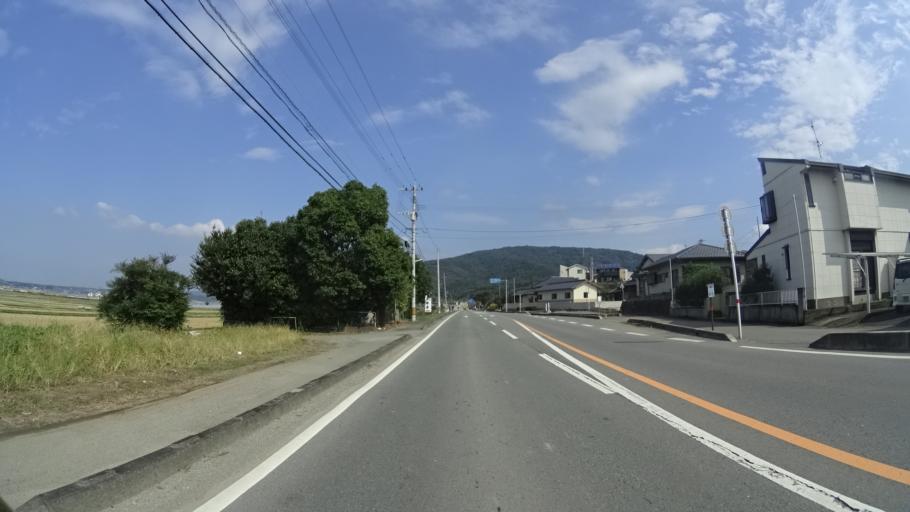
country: JP
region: Kumamoto
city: Ozu
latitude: 32.7565
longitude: 130.8077
